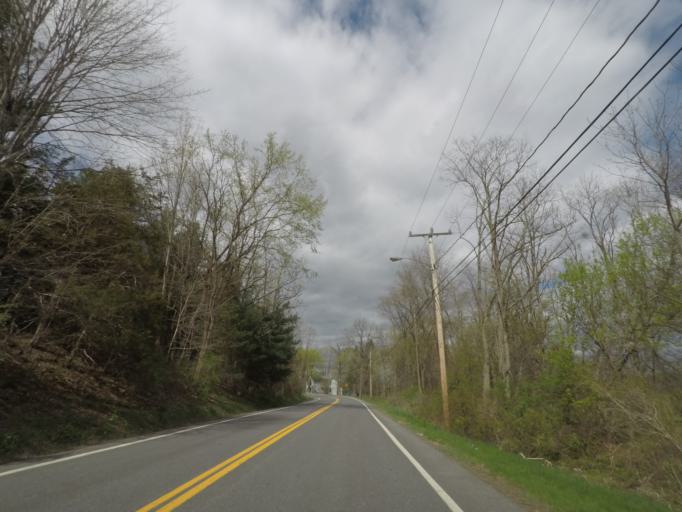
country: US
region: New York
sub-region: Columbia County
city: Philmont
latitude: 42.2570
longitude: -73.6648
